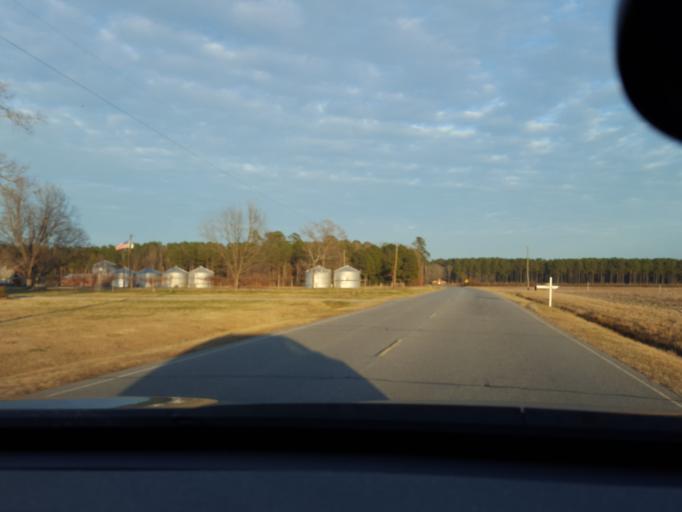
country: US
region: North Carolina
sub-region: Hertford County
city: Murfreesboro
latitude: 36.2763
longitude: -77.2105
